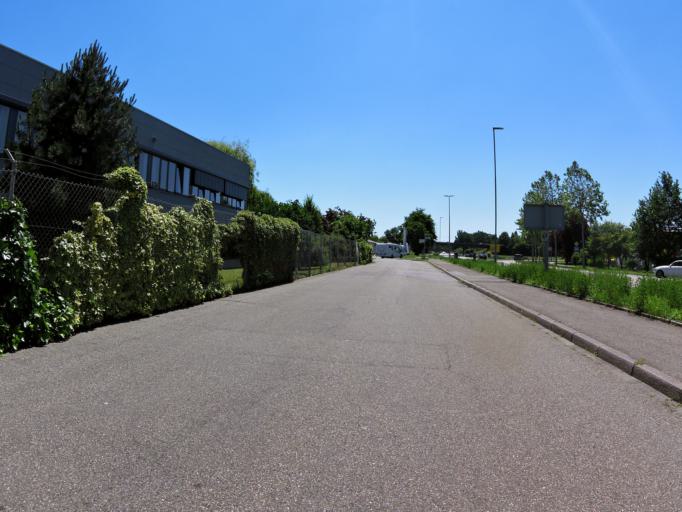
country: DE
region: Baden-Wuerttemberg
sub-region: Freiburg Region
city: Lahr
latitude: 48.3358
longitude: 7.8291
